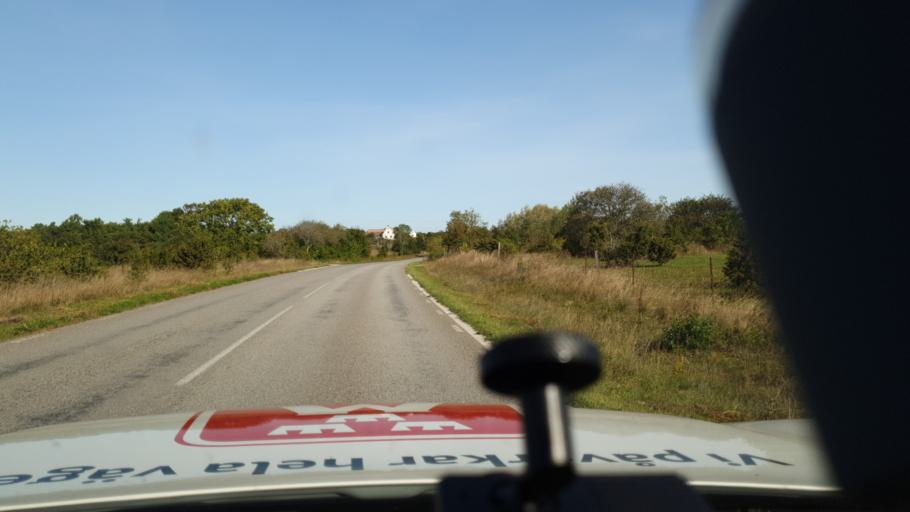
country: SE
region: Gotland
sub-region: Gotland
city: Slite
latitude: 57.9253
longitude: 19.1438
